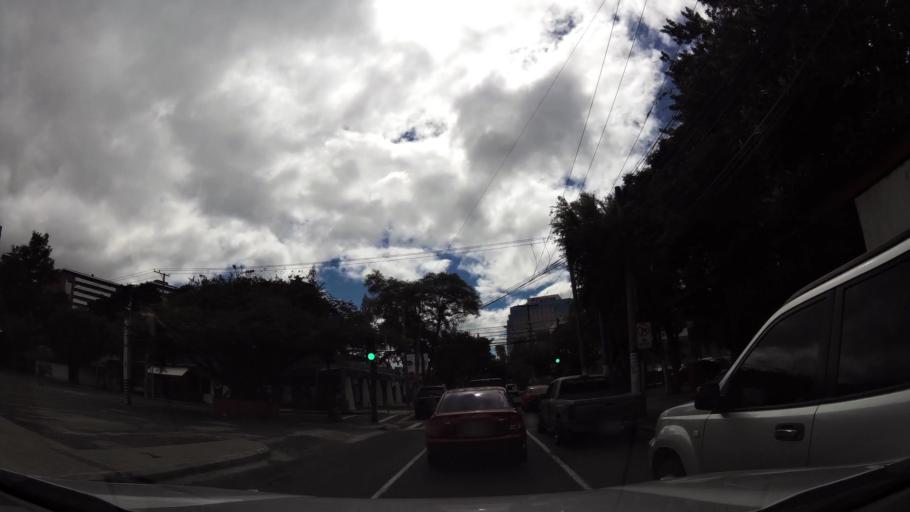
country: GT
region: Guatemala
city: Santa Catarina Pinula
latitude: 14.5950
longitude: -90.5115
